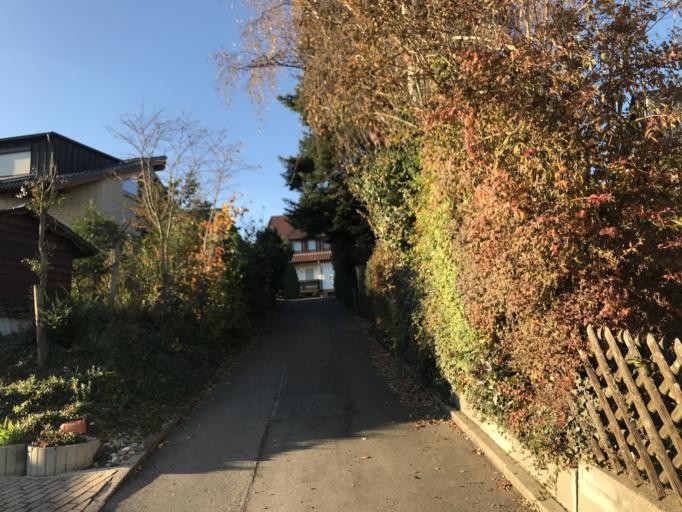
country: DE
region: Baden-Wuerttemberg
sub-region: Regierungsbezirk Stuttgart
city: Altenriet
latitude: 48.5886
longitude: 9.2166
